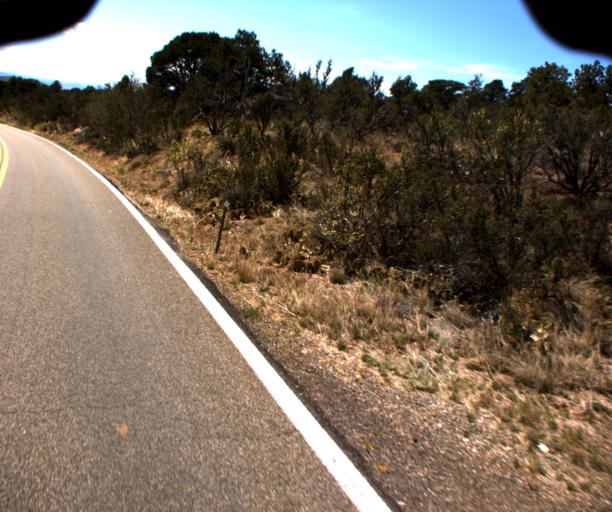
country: US
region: Arizona
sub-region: Yavapai County
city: Prescott Valley
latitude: 34.6788
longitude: -112.1909
